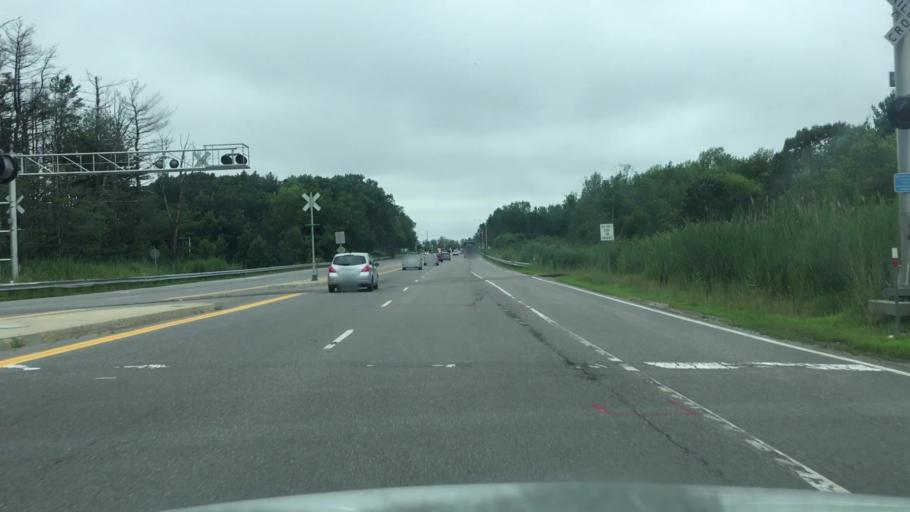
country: US
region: New Hampshire
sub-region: Rockingham County
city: Greenland
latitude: 43.0481
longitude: -70.8167
